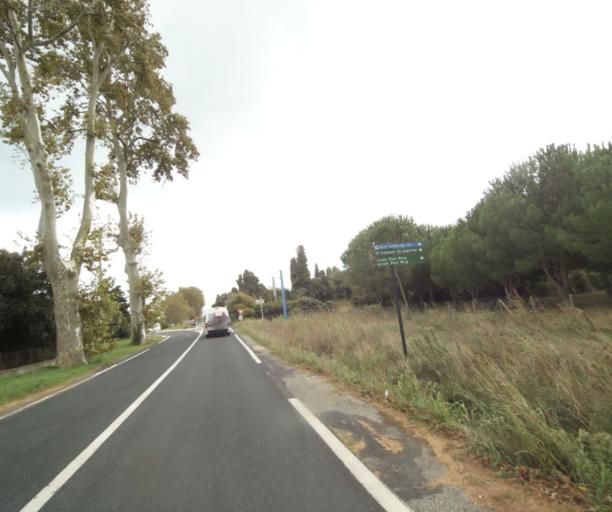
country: FR
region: Languedoc-Roussillon
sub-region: Departement des Pyrenees-Orientales
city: Elne
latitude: 42.5933
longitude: 2.9778
